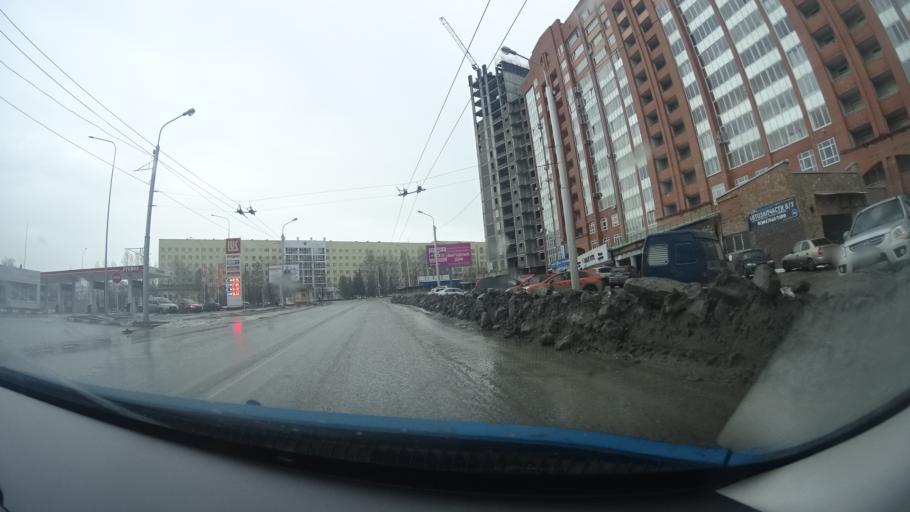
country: RU
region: Bashkortostan
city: Ufa
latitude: 54.7122
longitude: 55.9991
